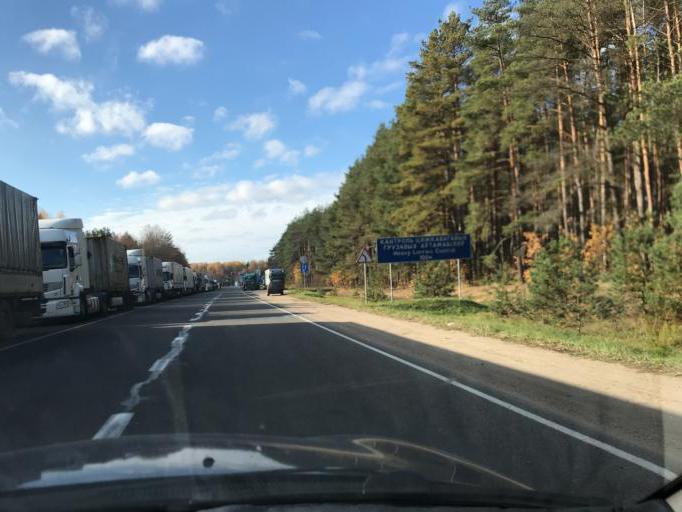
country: LT
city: Salcininkai
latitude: 54.2638
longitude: 25.3662
